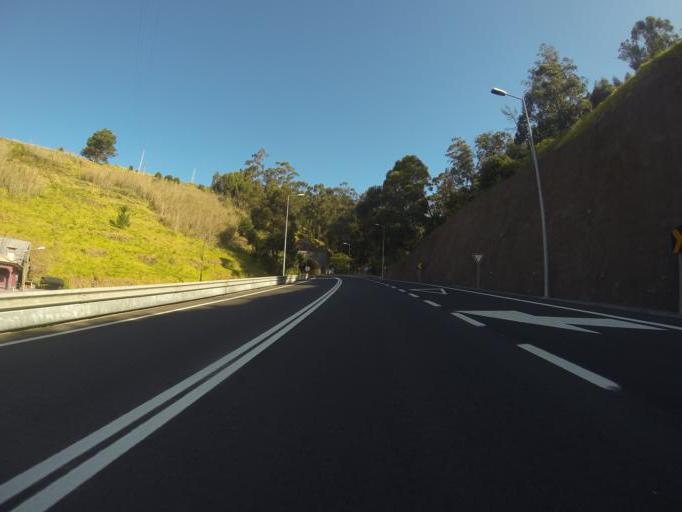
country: PT
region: Madeira
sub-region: Calheta
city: Estreito da Calheta
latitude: 32.7447
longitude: -17.1985
